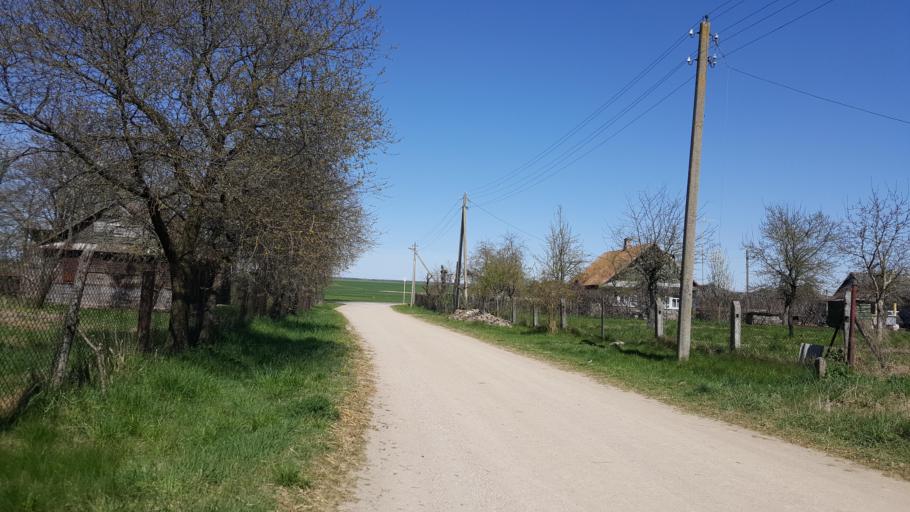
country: BY
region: Brest
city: Vysokaye
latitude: 52.3475
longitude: 23.5305
